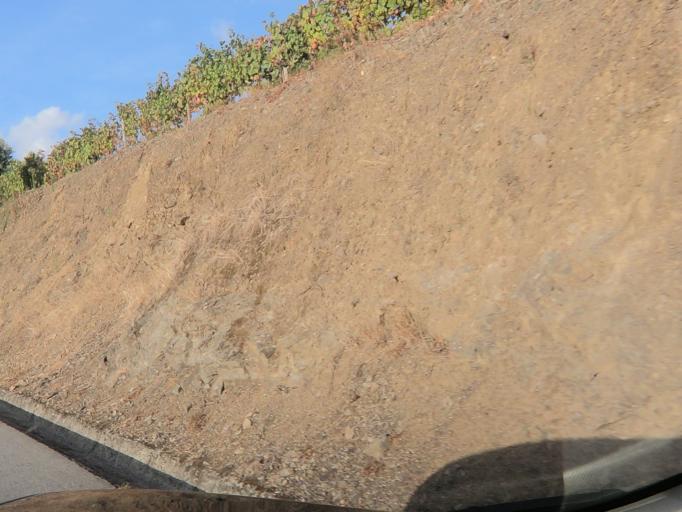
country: PT
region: Vila Real
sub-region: Santa Marta de Penaguiao
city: Santa Marta de Penaguiao
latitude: 41.2083
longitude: -7.8041
